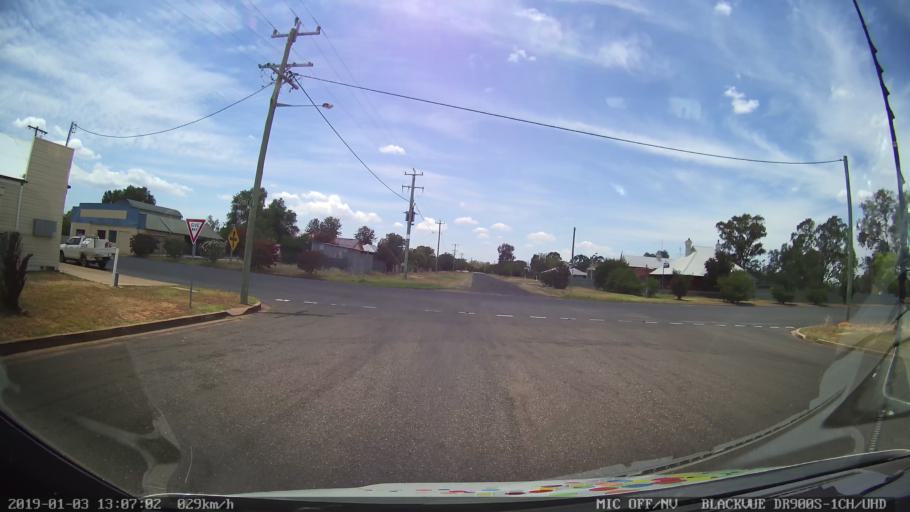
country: AU
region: New South Wales
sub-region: Cabonne
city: Canowindra
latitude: -33.6149
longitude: 148.4350
